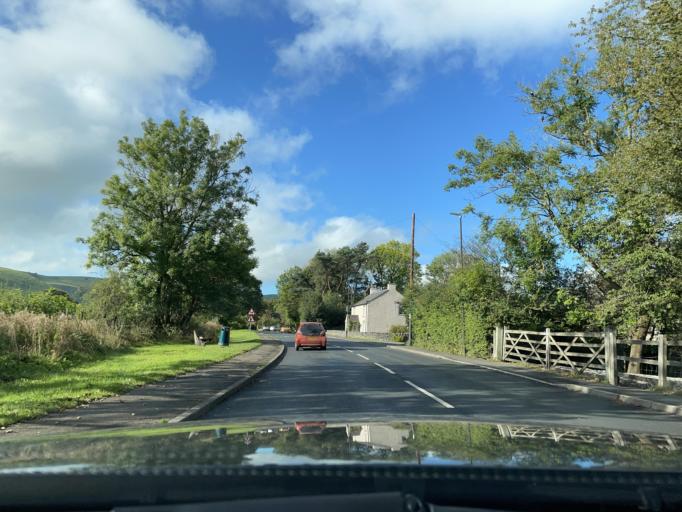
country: GB
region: England
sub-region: Derbyshire
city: Hope Valley
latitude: 53.3481
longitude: -1.7550
